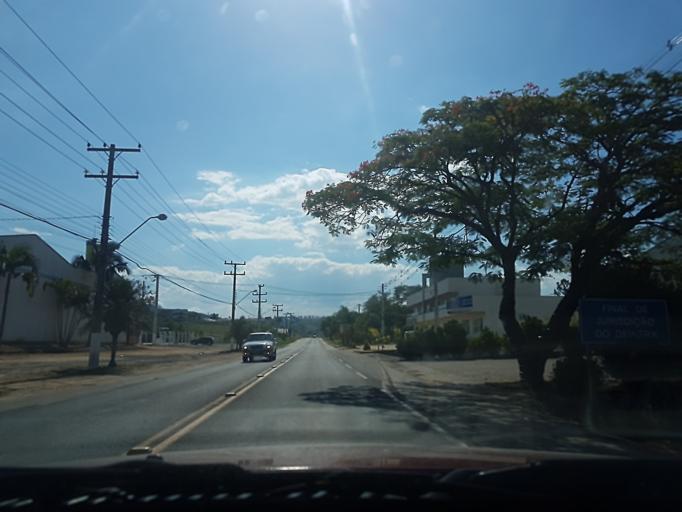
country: BR
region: Santa Catarina
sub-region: Braco Do Norte
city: Braco do Norte
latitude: -28.3235
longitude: -49.1661
